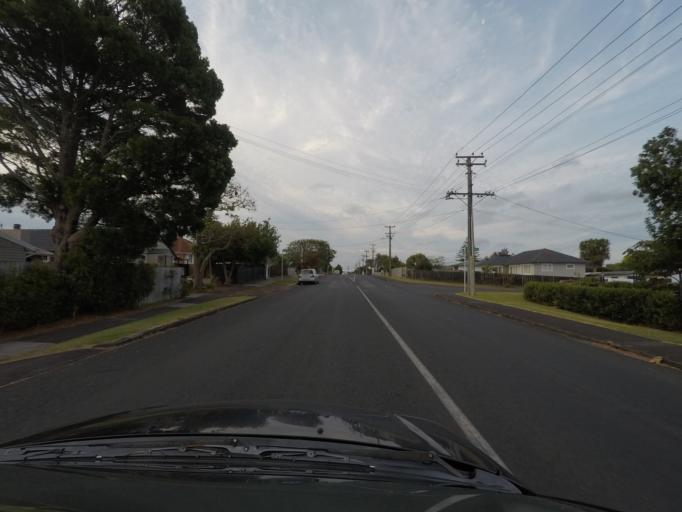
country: NZ
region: Auckland
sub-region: Auckland
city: Rosebank
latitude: -36.8364
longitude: 174.6503
